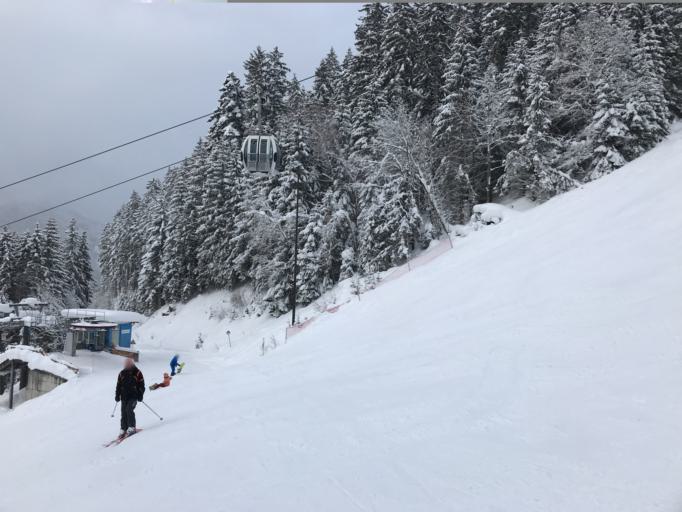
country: AT
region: Salzburg
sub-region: Politischer Bezirk Zell am See
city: Zell am See
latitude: 47.3208
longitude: 12.7848
